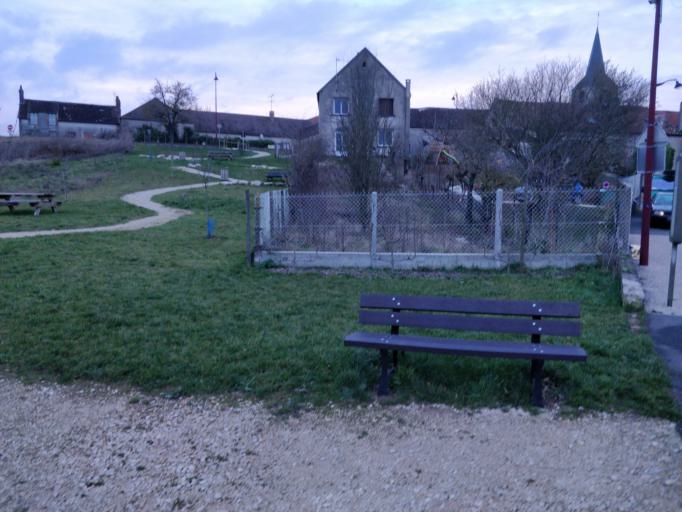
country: FR
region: Bourgogne
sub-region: Departement de l'Yonne
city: Gron
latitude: 48.1603
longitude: 3.2617
